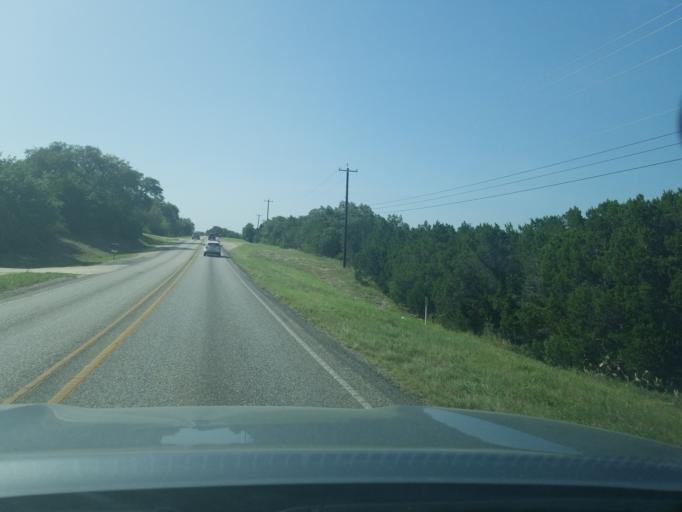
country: US
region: Texas
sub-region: Comal County
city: Garden Ridge
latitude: 29.6680
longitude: -98.3165
